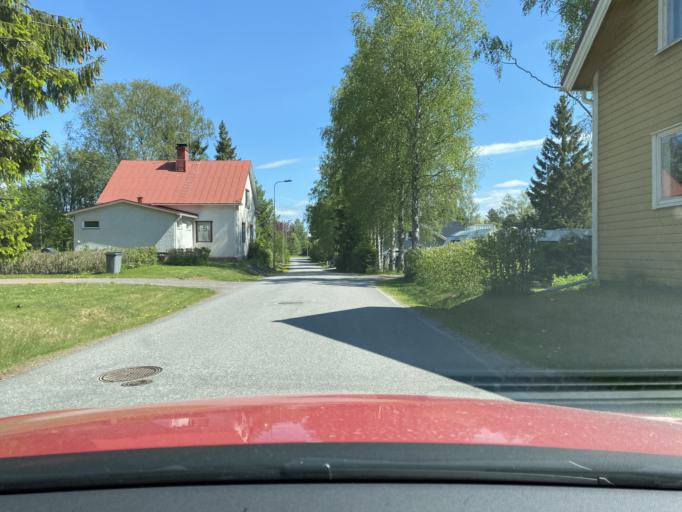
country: FI
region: Satakunta
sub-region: Rauma
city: Eura
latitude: 61.1109
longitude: 22.1413
